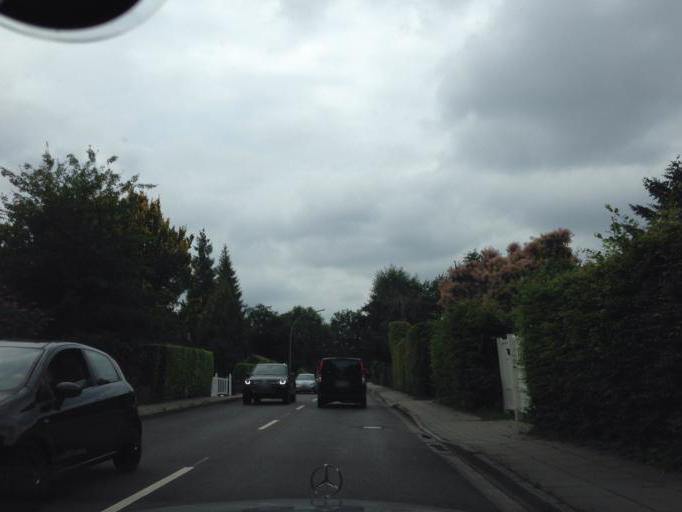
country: DE
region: Hamburg
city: Sasel
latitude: 53.6450
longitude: 10.1218
